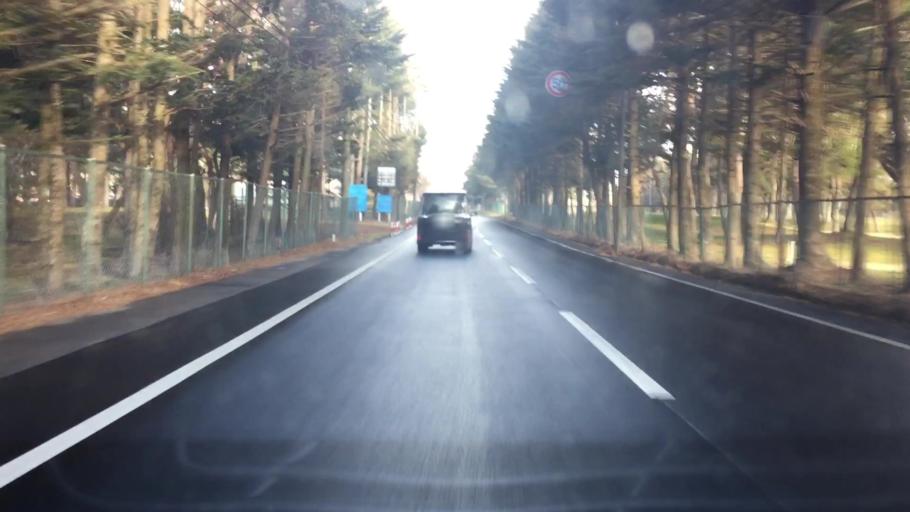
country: JP
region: Nagano
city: Saku
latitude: 36.3040
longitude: 138.6319
